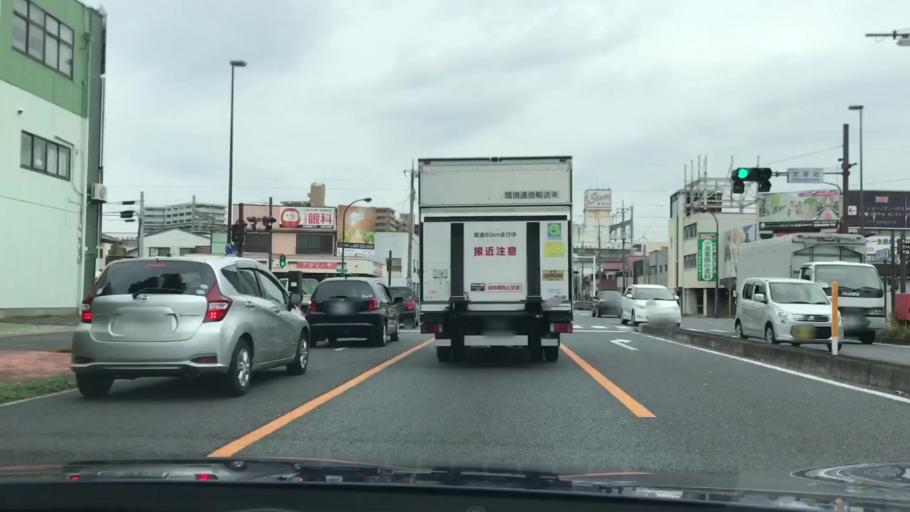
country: JP
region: Gunma
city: Takasaki
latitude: 36.3334
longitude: 139.0140
